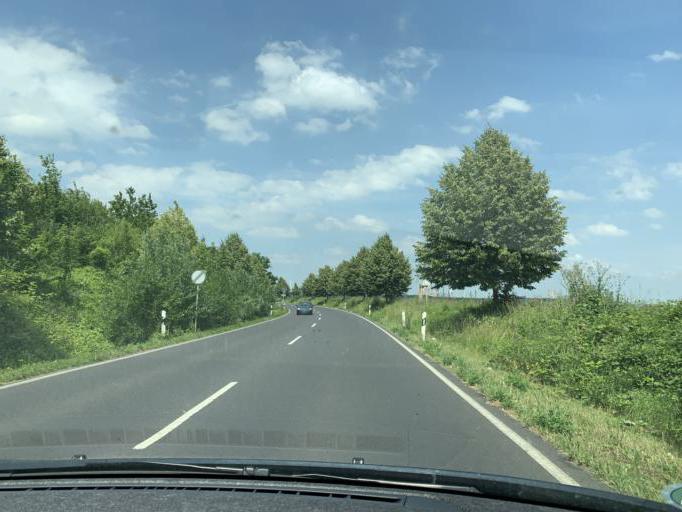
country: DE
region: North Rhine-Westphalia
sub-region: Regierungsbezirk Koln
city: Bedburg
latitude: 50.9945
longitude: 6.5872
